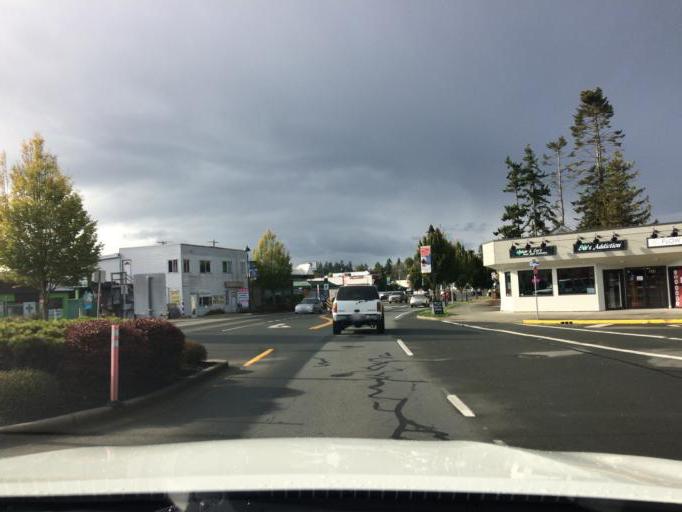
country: CA
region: British Columbia
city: Campbell River
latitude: 49.9708
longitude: -125.2157
